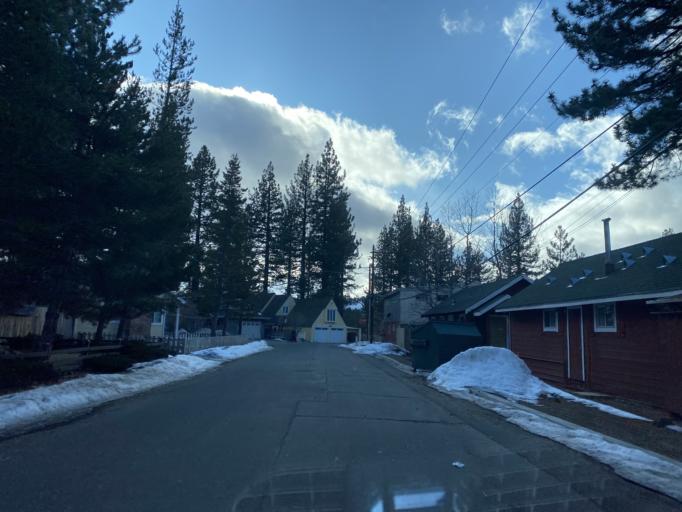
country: US
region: California
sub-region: El Dorado County
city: South Lake Tahoe
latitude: 38.9229
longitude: -119.9888
